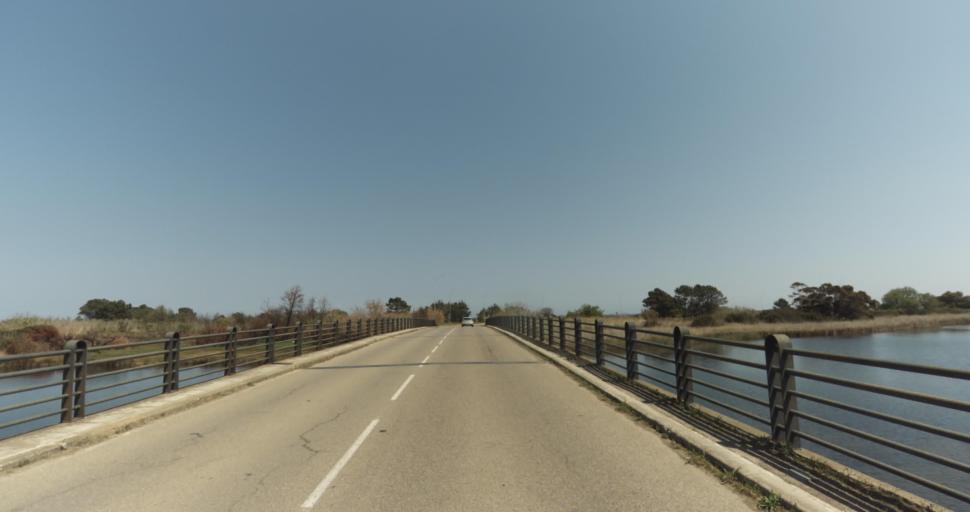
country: FR
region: Corsica
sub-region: Departement de la Haute-Corse
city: Biguglia
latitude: 42.6545
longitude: 9.4478
